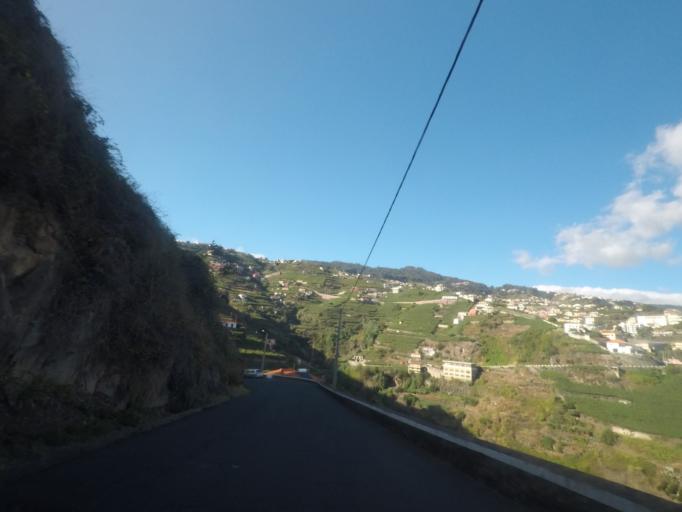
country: PT
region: Madeira
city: Camara de Lobos
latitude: 32.6683
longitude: -16.9866
